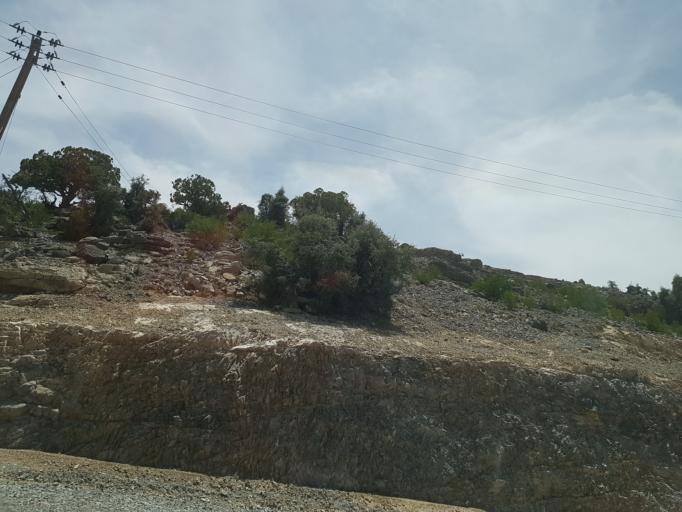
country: OM
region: Muhafazat ad Dakhiliyah
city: Nizwa
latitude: 23.1134
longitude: 57.6499
